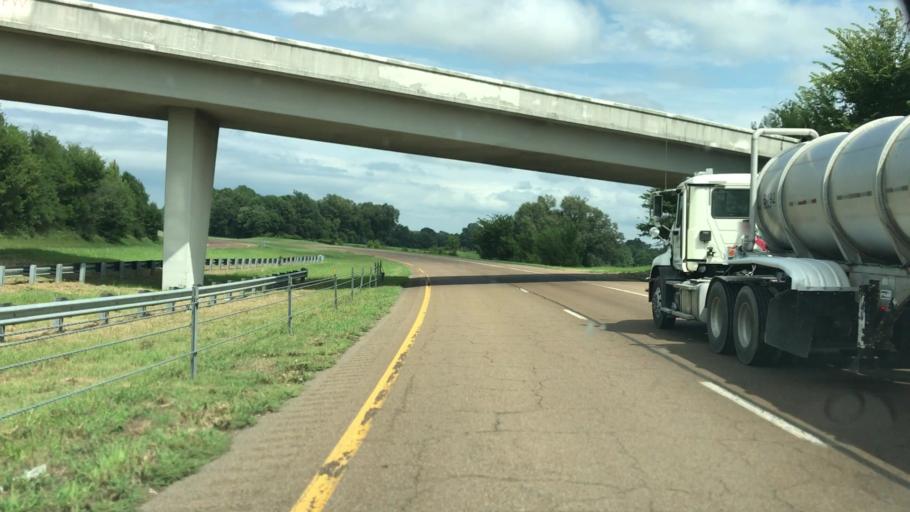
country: US
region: Tennessee
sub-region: Obion County
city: Union City
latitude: 36.4587
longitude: -88.9886
